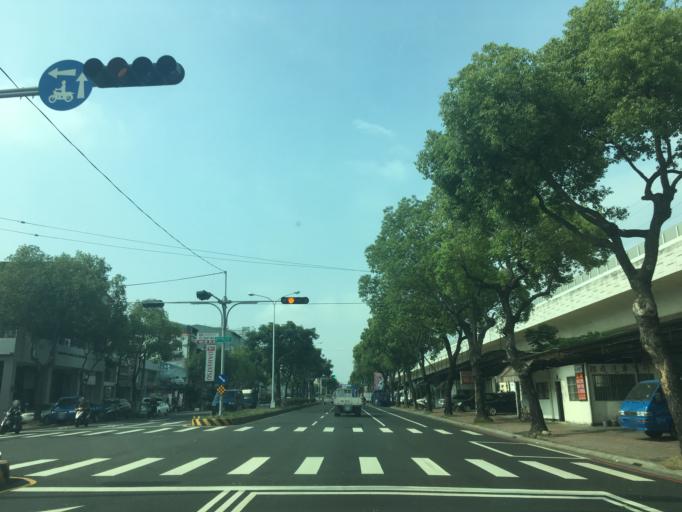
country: TW
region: Taiwan
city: Fengyuan
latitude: 24.2226
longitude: 120.7069
